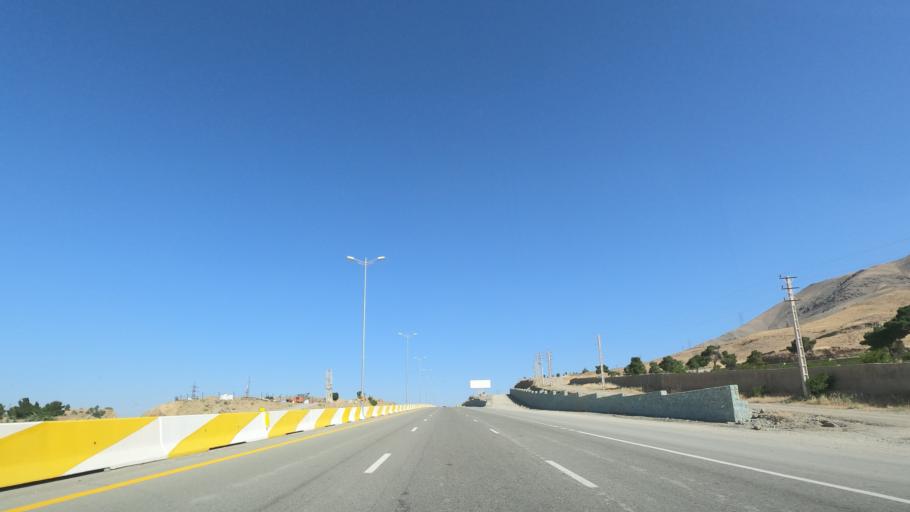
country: IR
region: Tehran
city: Shahr-e Qods
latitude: 35.7643
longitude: 51.0702
